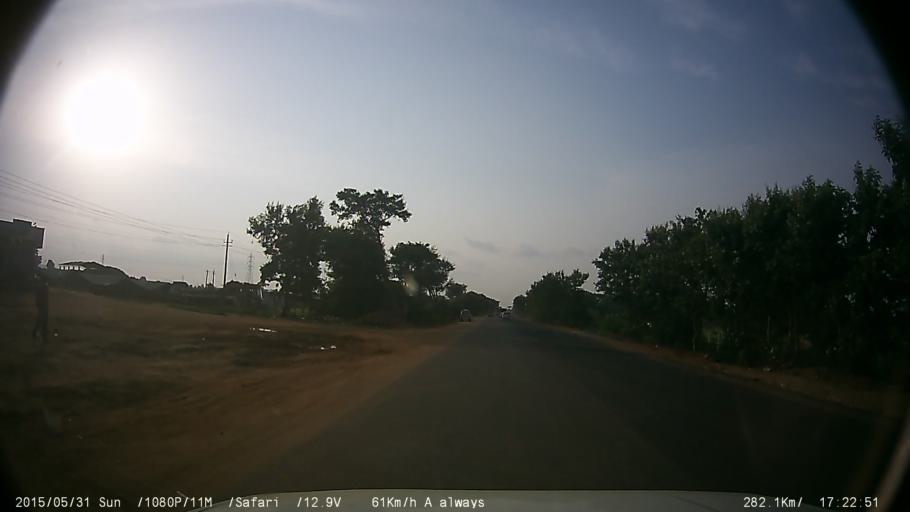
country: IN
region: Karnataka
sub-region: Chamrajnagar
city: Gundlupet
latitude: 11.8343
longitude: 76.6767
